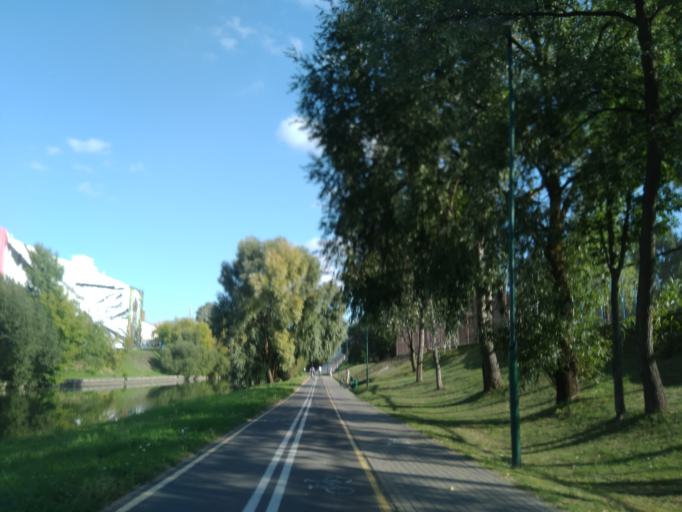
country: BY
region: Minsk
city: Minsk
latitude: 53.8891
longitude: 27.5695
